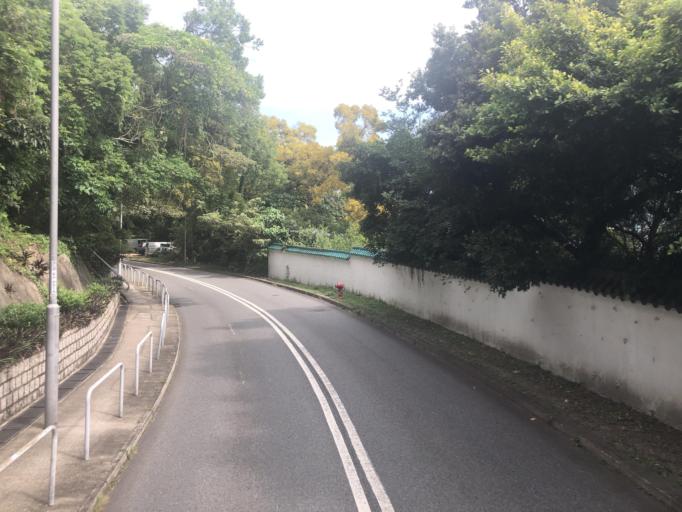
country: HK
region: Sai Kung
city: Sai Kung
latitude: 22.3898
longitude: 114.2912
